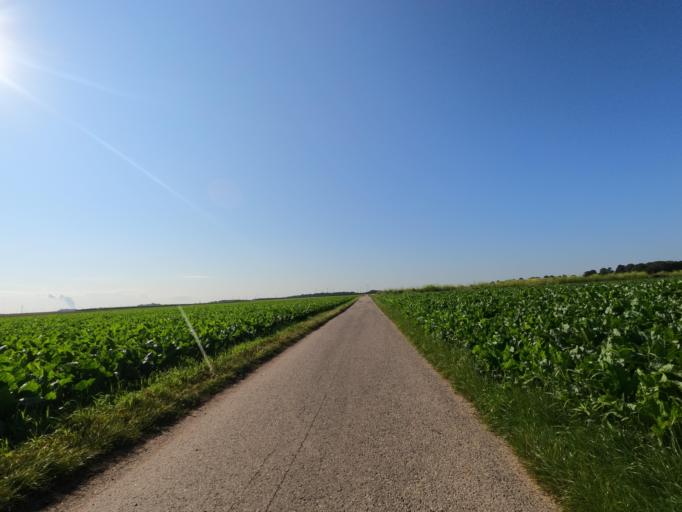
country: DE
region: North Rhine-Westphalia
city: Erkelenz
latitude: 51.0702
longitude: 6.3566
